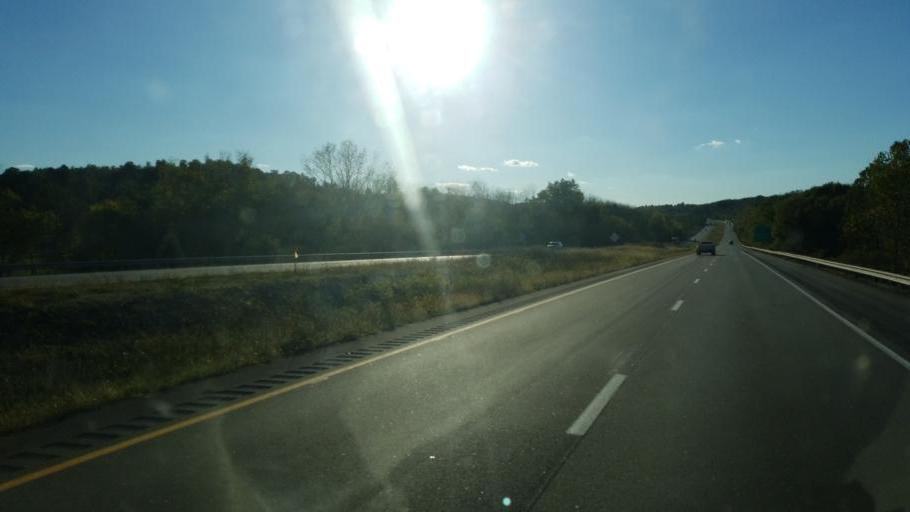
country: US
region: Ohio
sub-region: Guernsey County
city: Byesville
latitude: 40.0037
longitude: -81.5156
